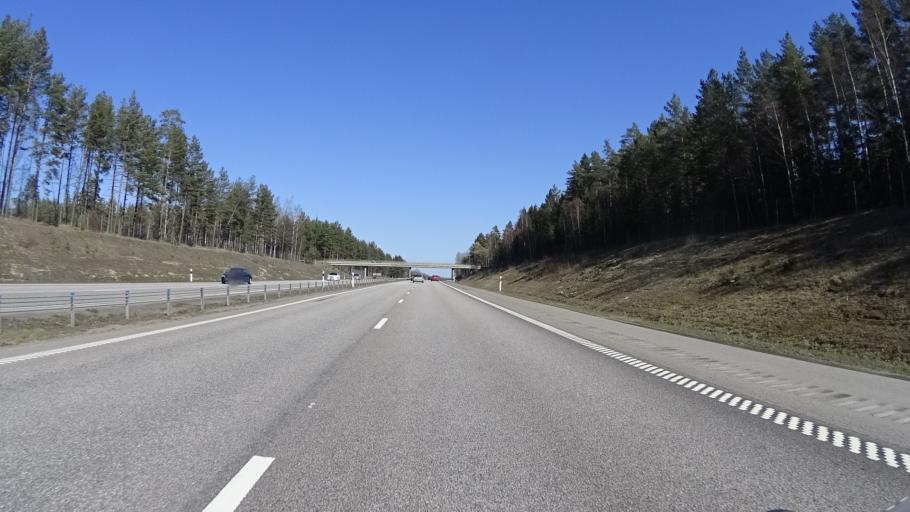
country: SE
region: OEstergoetland
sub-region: Mjolby Kommun
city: Mjolby
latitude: 58.3479
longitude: 15.1908
